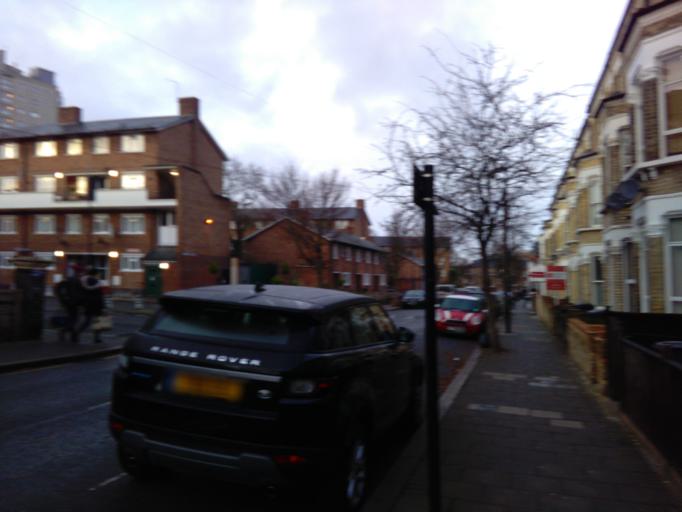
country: GB
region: England
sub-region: Greater London
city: Brixton Hill
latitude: 51.4624
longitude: -0.1269
